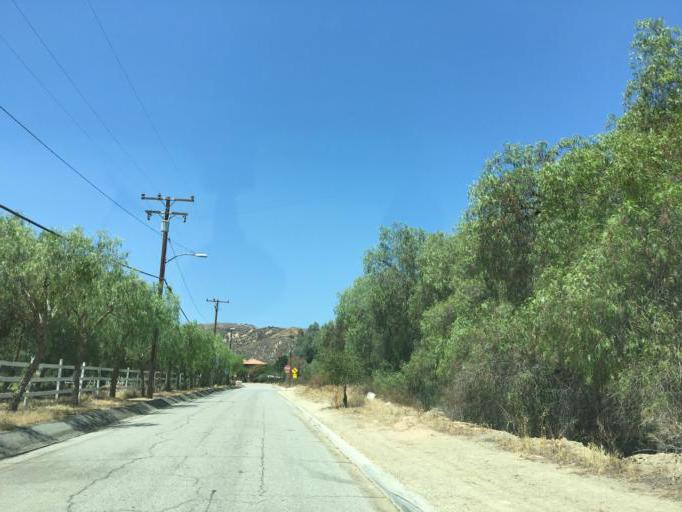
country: US
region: California
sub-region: Los Angeles County
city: Val Verde
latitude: 34.4493
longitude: -118.6776
